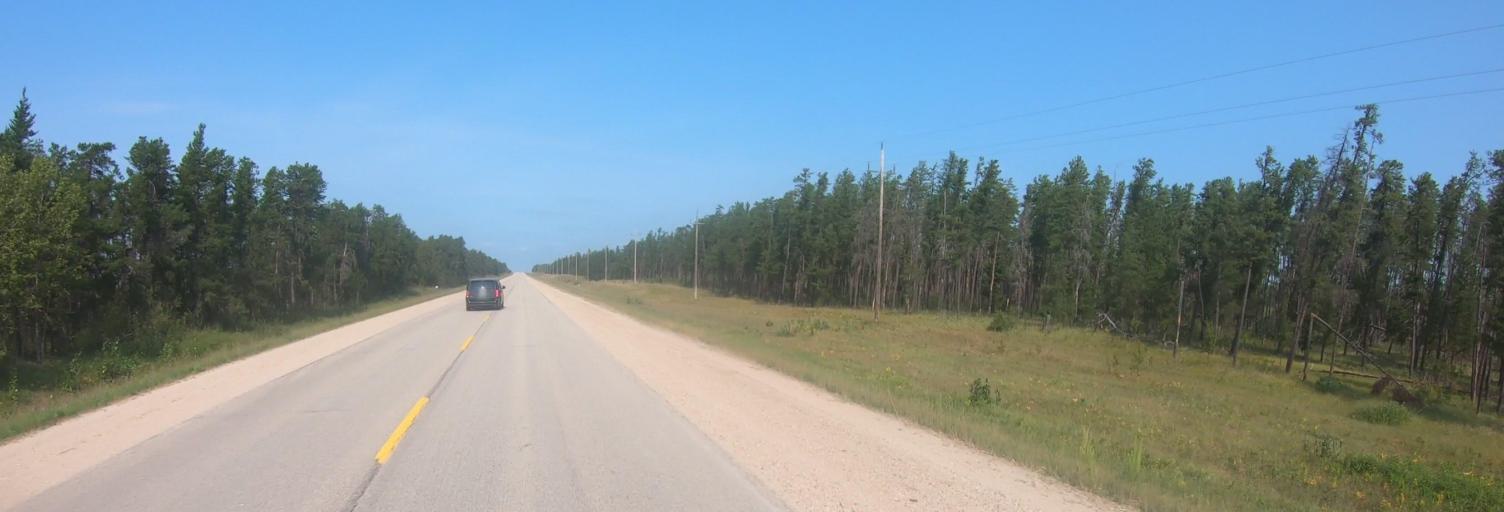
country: US
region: Minnesota
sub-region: Roseau County
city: Roseau
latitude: 49.1263
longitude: -96.0699
